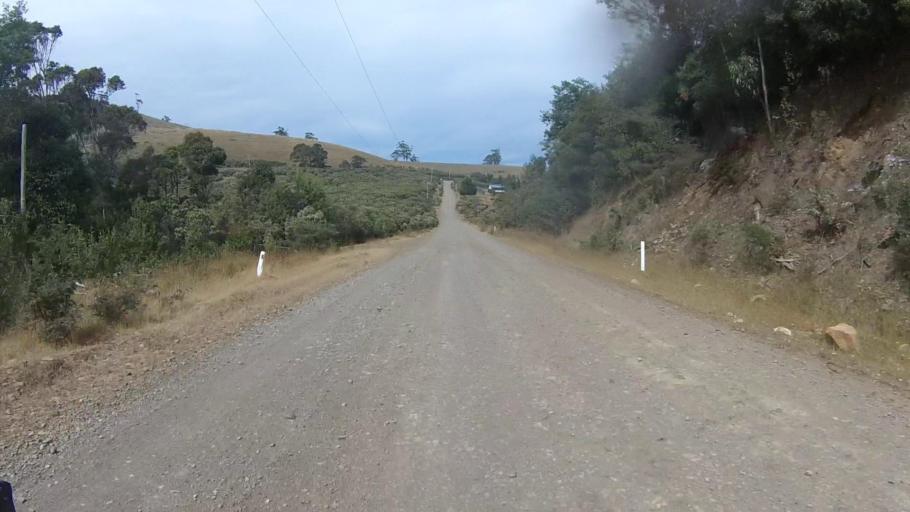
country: AU
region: Tasmania
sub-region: Sorell
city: Sorell
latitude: -42.7741
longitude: 147.8300
